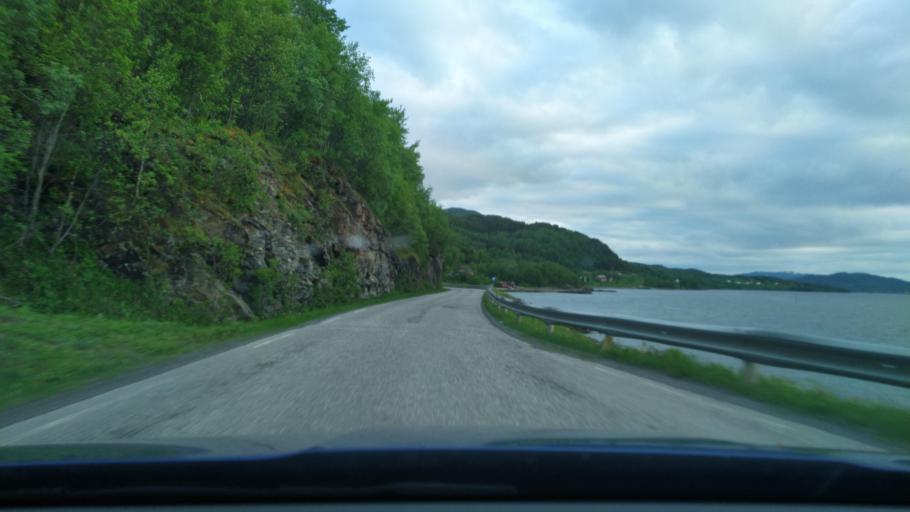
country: NO
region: Troms
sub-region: Lenvik
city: Finnsnes
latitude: 69.1401
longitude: 17.9105
